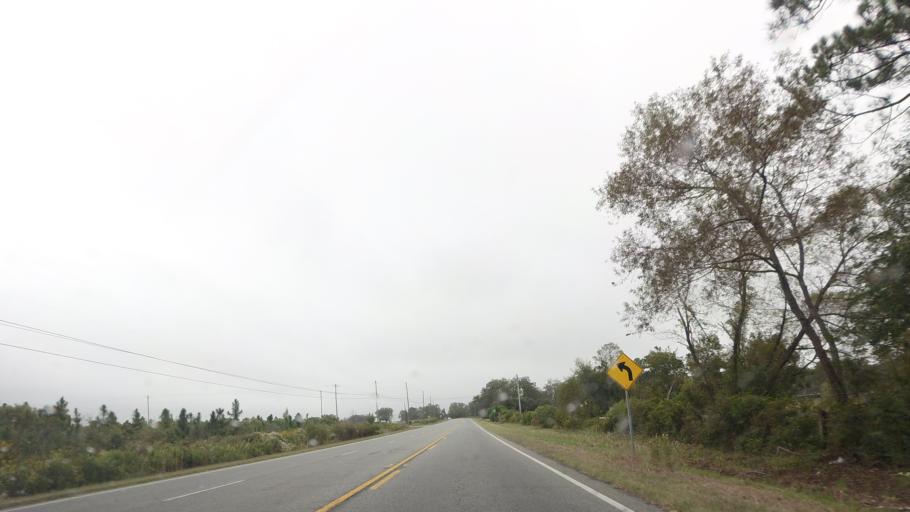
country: US
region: Georgia
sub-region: Ben Hill County
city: Fitzgerald
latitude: 31.6783
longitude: -83.2367
